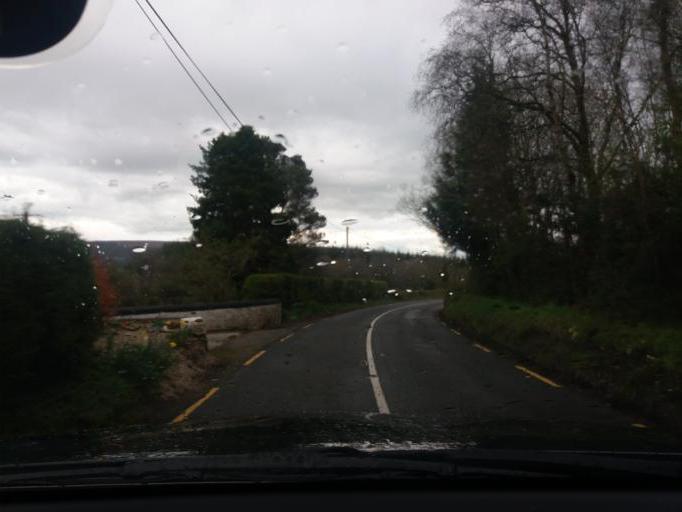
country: IE
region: Ulster
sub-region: An Cabhan
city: Ballyconnell
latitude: 54.1554
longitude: -7.7261
